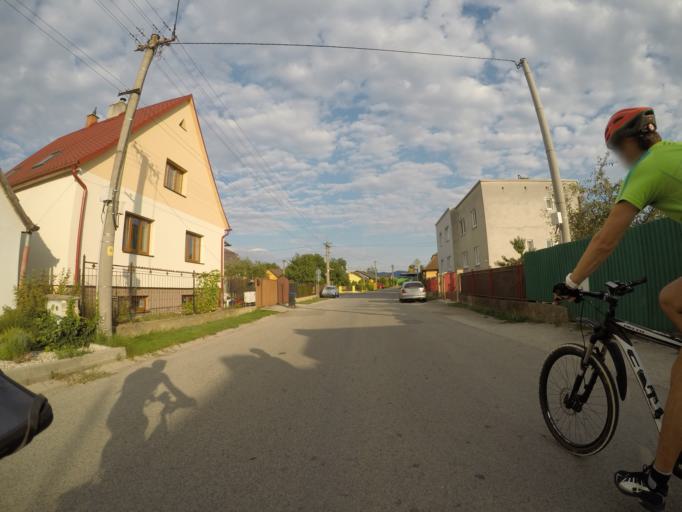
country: SK
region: Trenciansky
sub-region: Okres Trencin
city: Trencin
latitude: 48.8935
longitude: 17.9975
